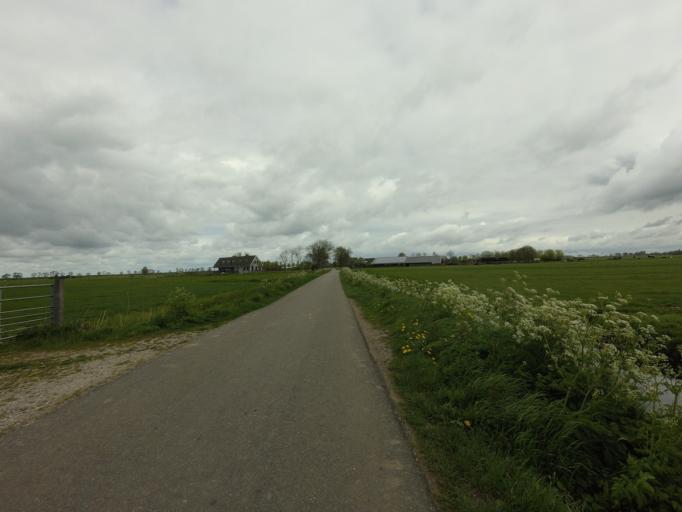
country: NL
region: North Holland
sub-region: Gemeente Weesp
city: Weesp
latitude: 52.3316
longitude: 5.0786
